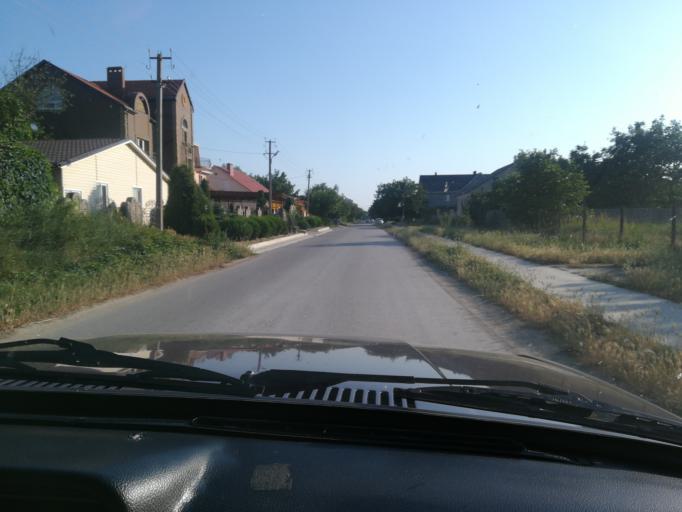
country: RU
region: Krasnodarskiy
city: Vityazevo
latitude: 45.0069
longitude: 37.2931
